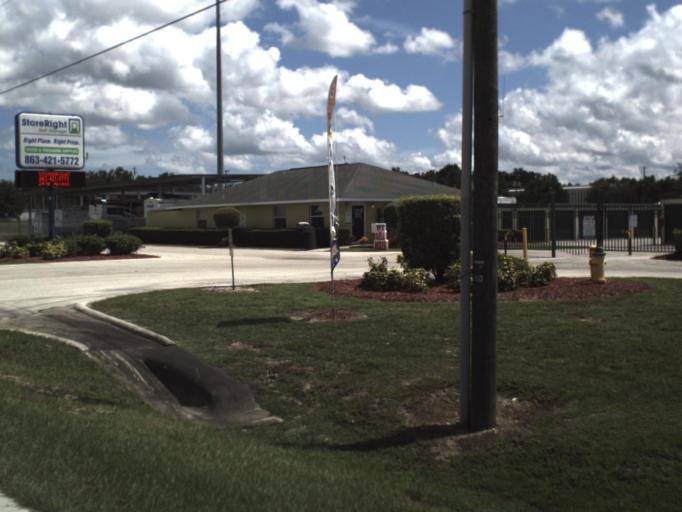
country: US
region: Florida
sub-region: Polk County
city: Lake Hamilton
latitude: 28.0808
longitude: -81.6597
